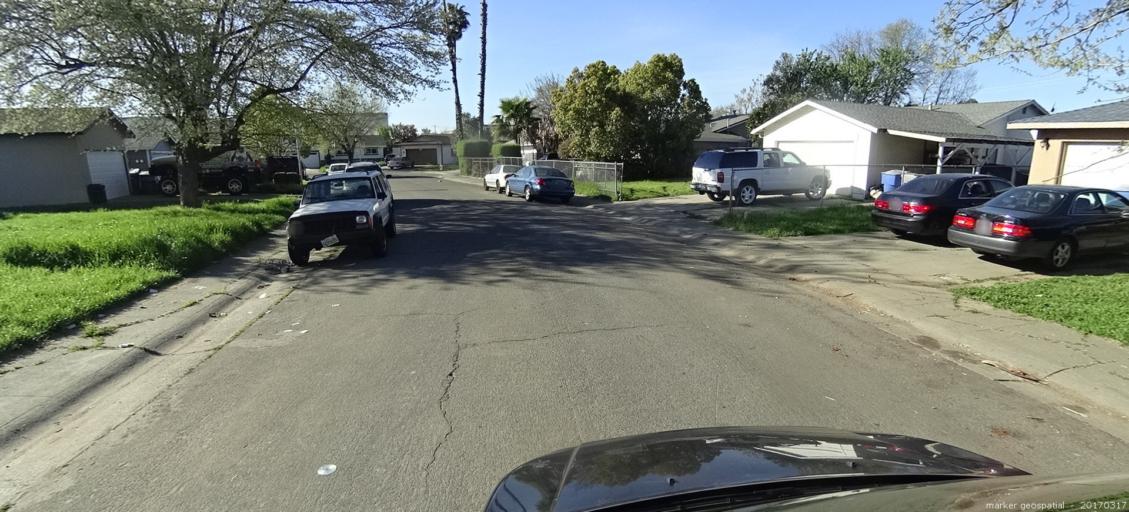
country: US
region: California
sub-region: Sacramento County
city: Parkway
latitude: 38.4845
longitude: -121.5043
